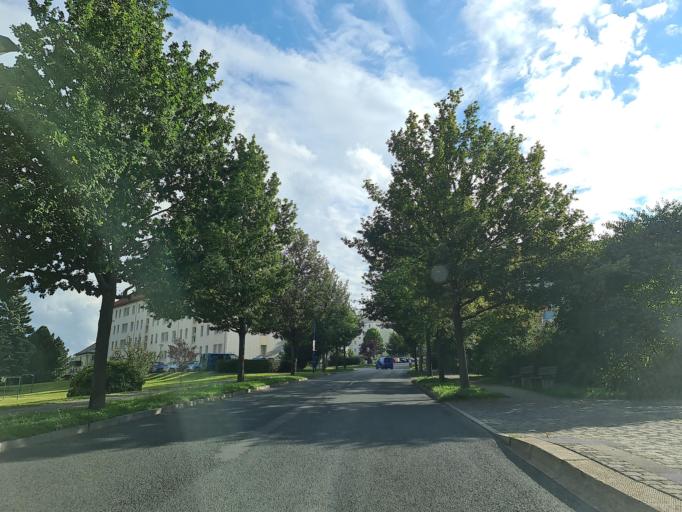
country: DE
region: Saxony
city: Auerbach
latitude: 50.5162
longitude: 12.3854
